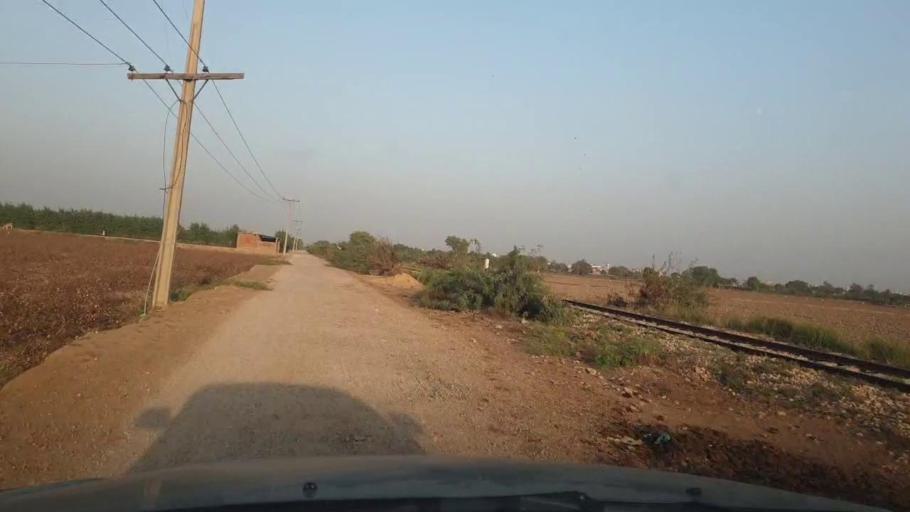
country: PK
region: Sindh
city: Tando Jam
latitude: 25.4260
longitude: 68.5128
